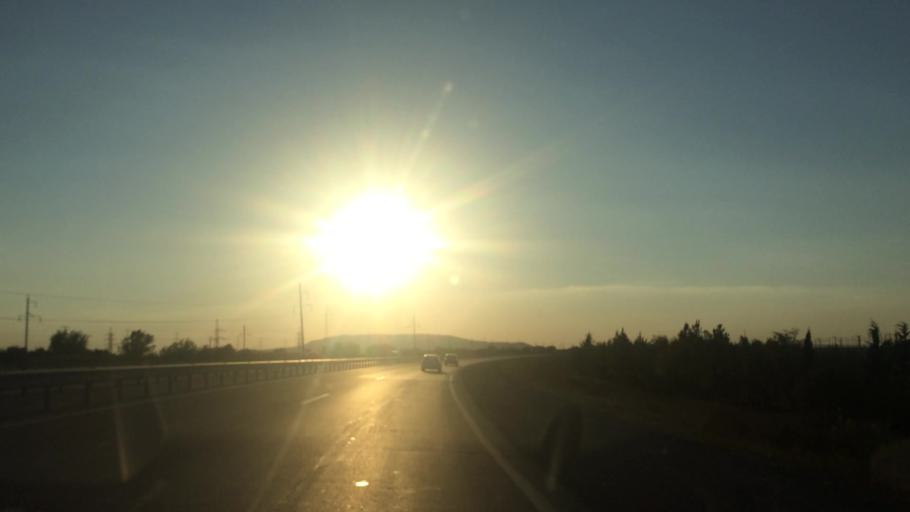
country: AZ
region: Baki
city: Qobustan
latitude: 39.9465
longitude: 49.3602
